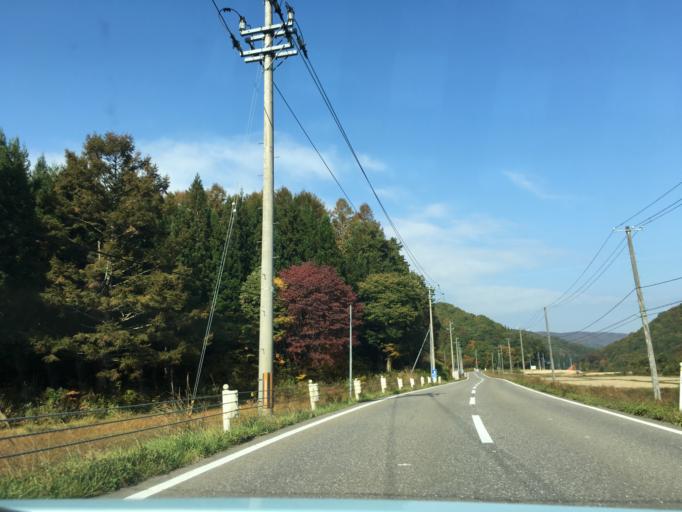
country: JP
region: Fukushima
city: Inawashiro
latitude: 37.4240
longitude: 140.0305
